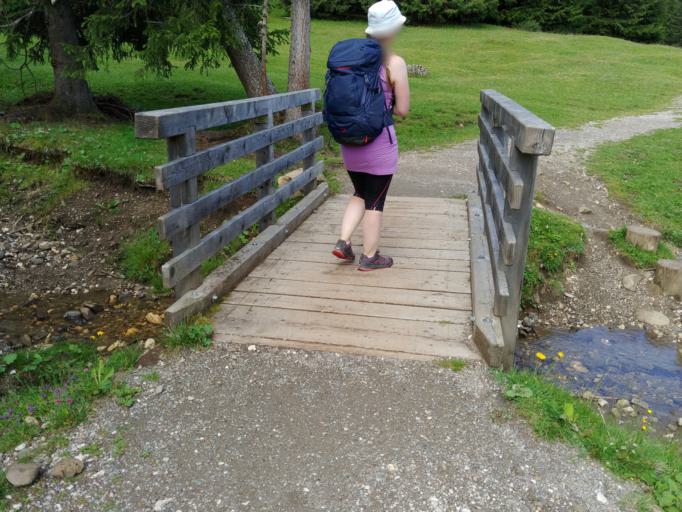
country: IT
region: Trentino-Alto Adige
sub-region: Bolzano
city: Santa Cristina Valgardena
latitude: 46.5463
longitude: 11.7195
